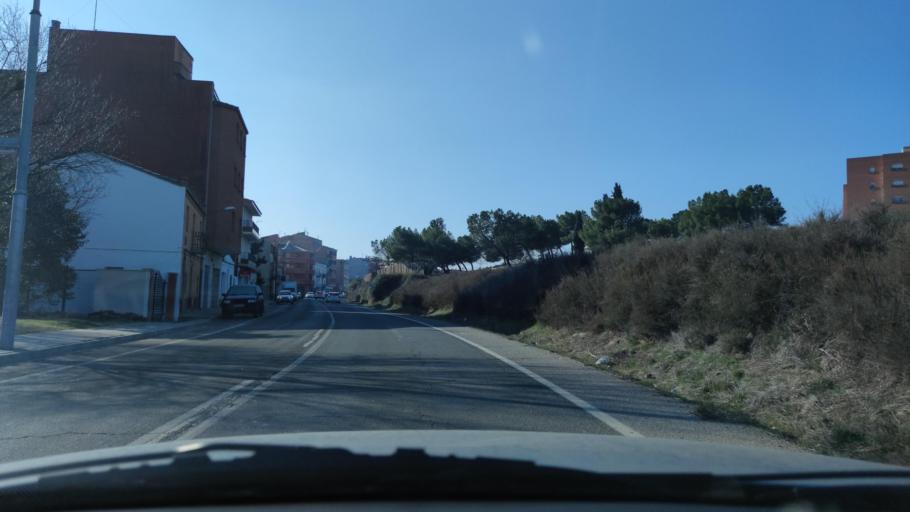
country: ES
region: Catalonia
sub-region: Provincia de Lleida
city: Lleida
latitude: 41.6307
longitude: 0.6336
